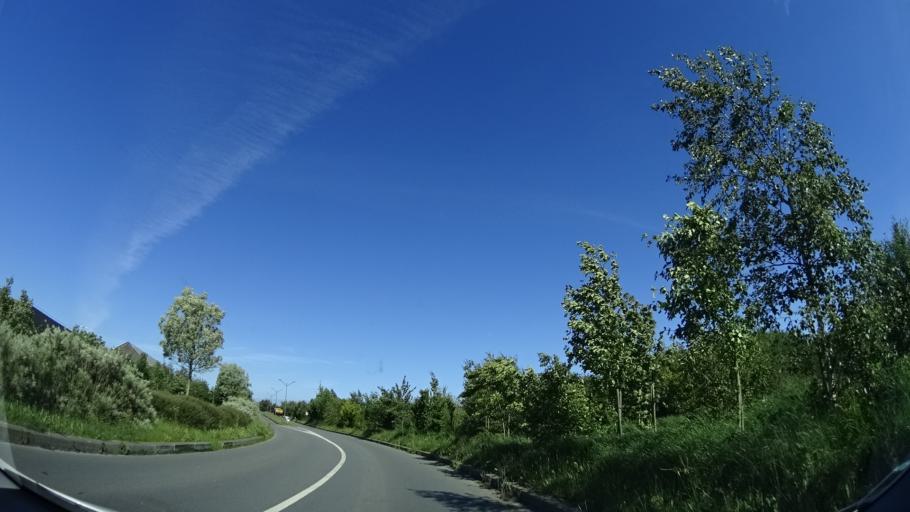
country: FR
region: Brittany
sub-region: Departement d'Ille-et-Vilaine
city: Saint-Jouan-des-Guerets
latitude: 48.6118
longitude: -1.9708
